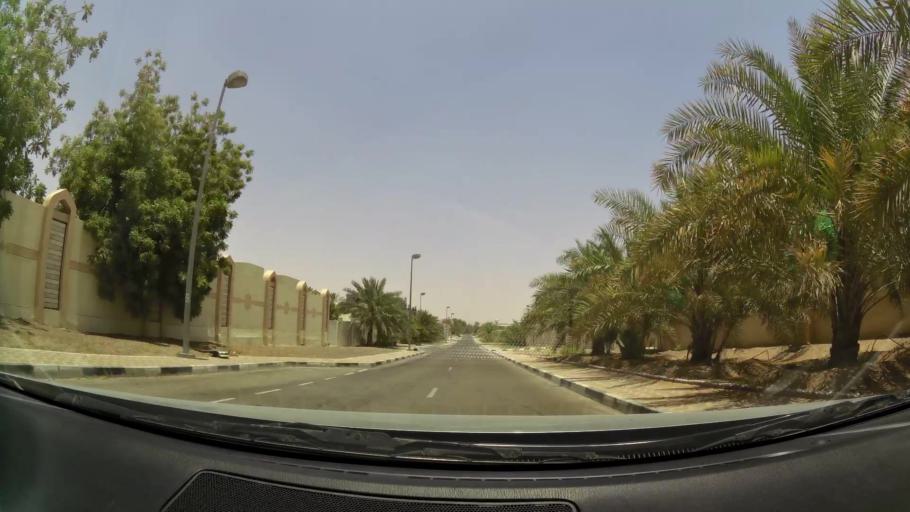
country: OM
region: Al Buraimi
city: Al Buraymi
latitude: 24.2688
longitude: 55.7272
